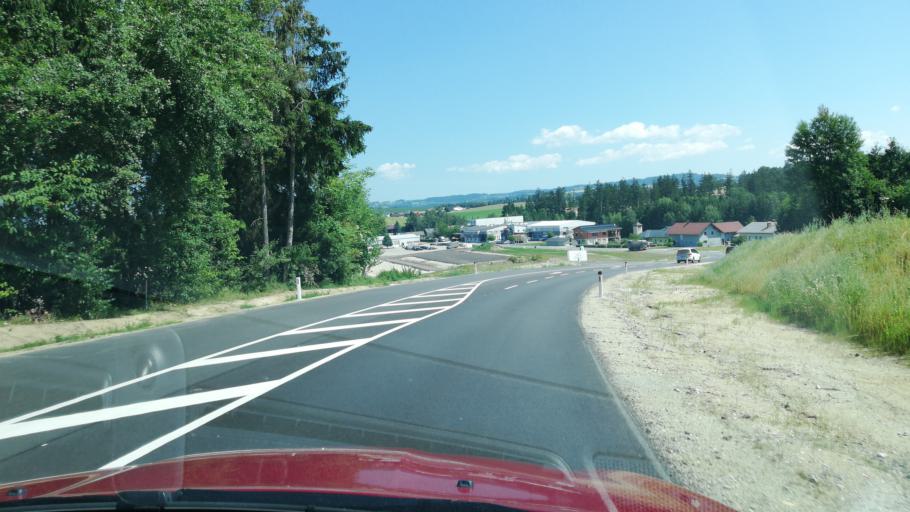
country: AT
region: Upper Austria
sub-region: Politischer Bezirk Rohrbach
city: Kleinzell im Muehlkreis
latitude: 48.4377
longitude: 14.0475
